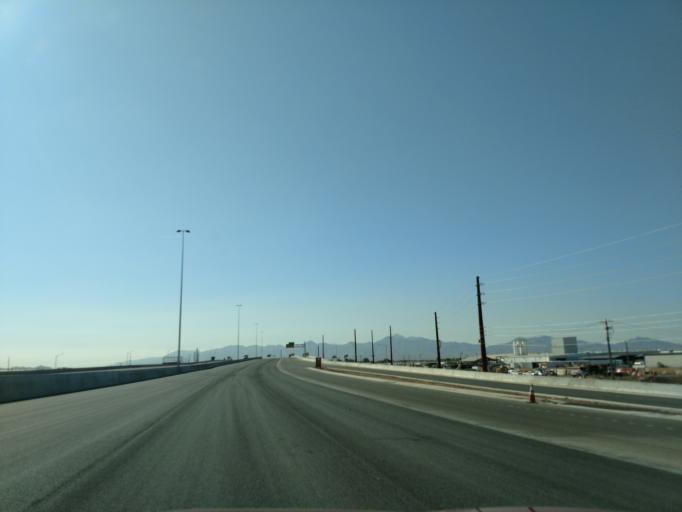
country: US
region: Arizona
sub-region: Maricopa County
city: Tolleson
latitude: 33.4484
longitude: -112.1872
